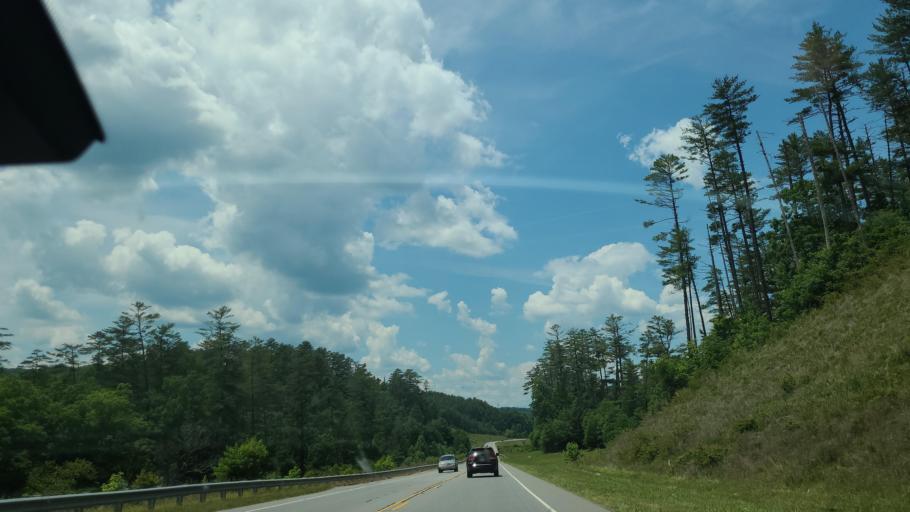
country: US
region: North Carolina
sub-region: Cherokee County
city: Murphy
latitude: 35.0709
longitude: -84.0161
